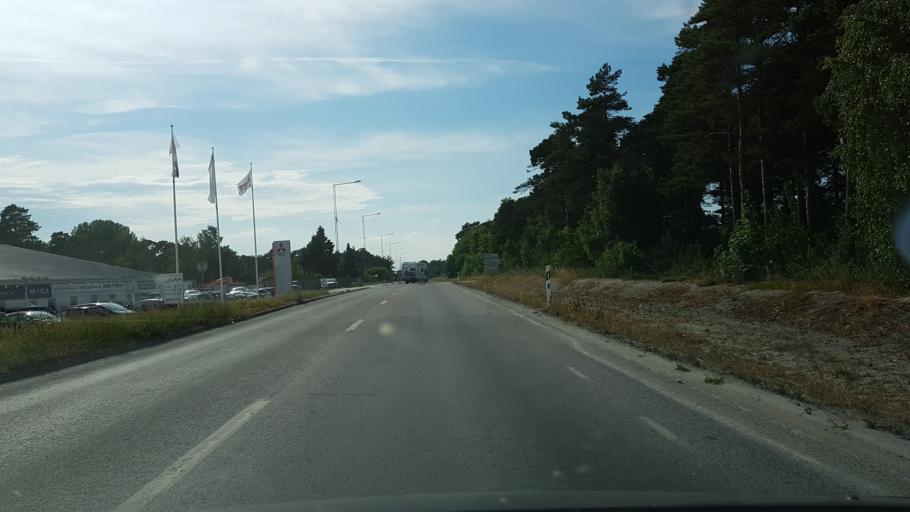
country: SE
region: Gotland
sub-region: Gotland
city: Visby
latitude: 57.6305
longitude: 18.3424
